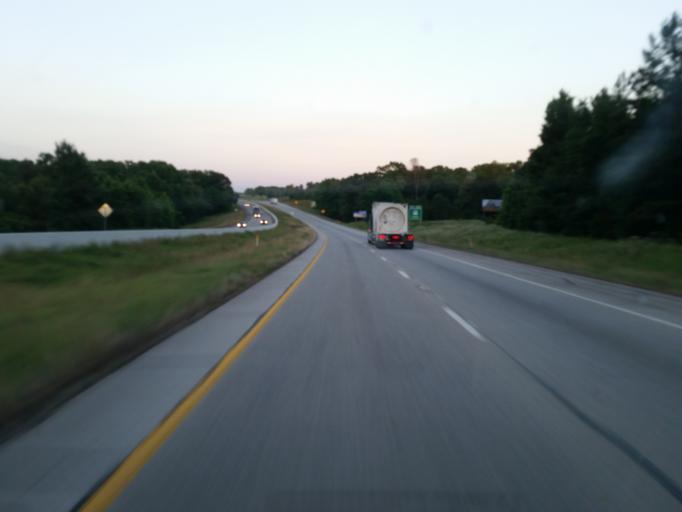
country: US
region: Texas
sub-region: Smith County
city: Hideaway
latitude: 32.4711
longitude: -95.4637
